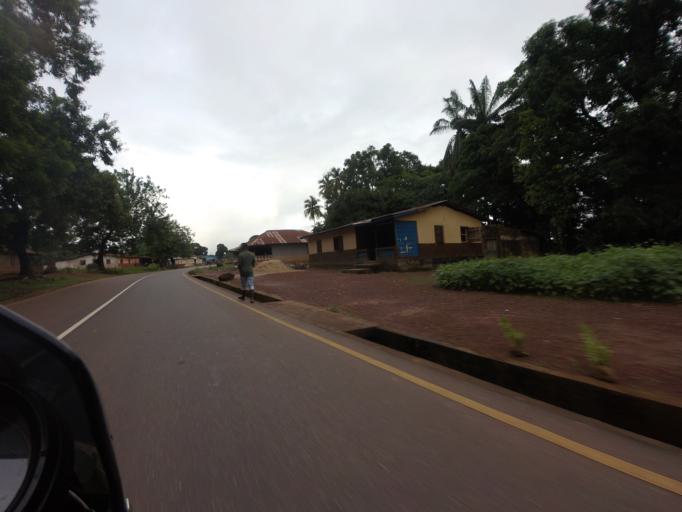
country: SL
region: Northern Province
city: Kambia
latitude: 9.1270
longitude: -12.9105
